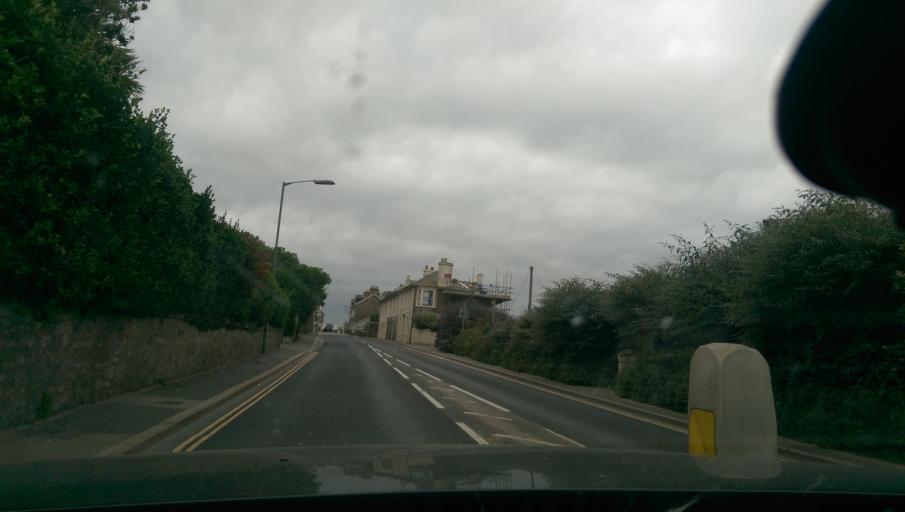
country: GB
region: England
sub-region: Cornwall
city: Marazion
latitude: 50.1251
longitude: -5.4767
